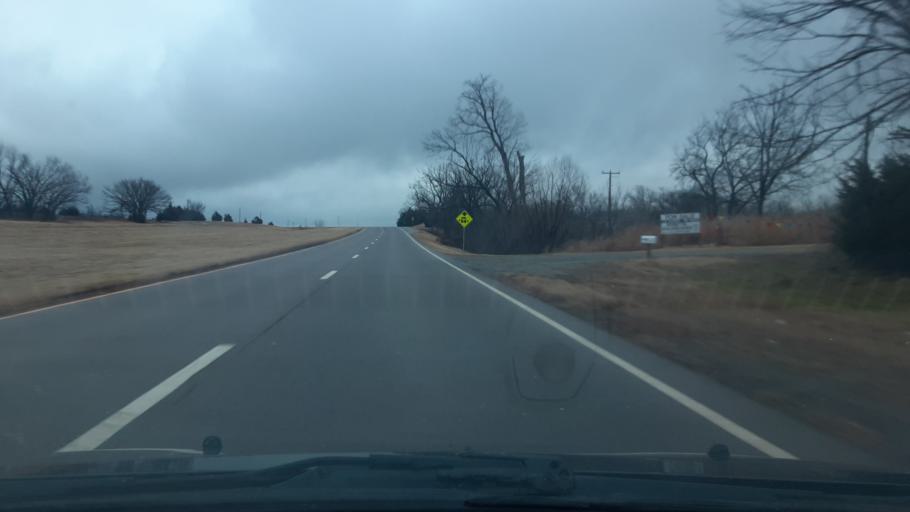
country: US
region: Oklahoma
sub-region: Payne County
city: Stillwater
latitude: 36.1158
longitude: -97.1520
